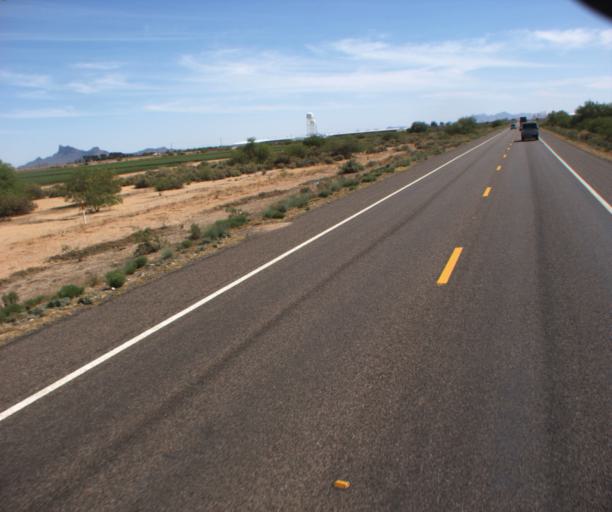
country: US
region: Arizona
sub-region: Pinal County
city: Eloy
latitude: 32.7454
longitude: -111.5159
